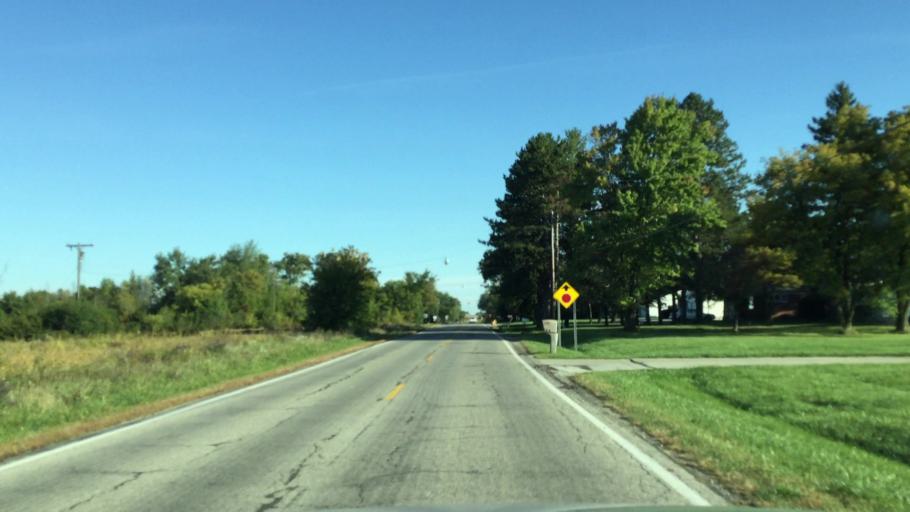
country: US
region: Michigan
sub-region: Genesee County
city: Beecher
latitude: 43.0878
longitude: -83.7536
